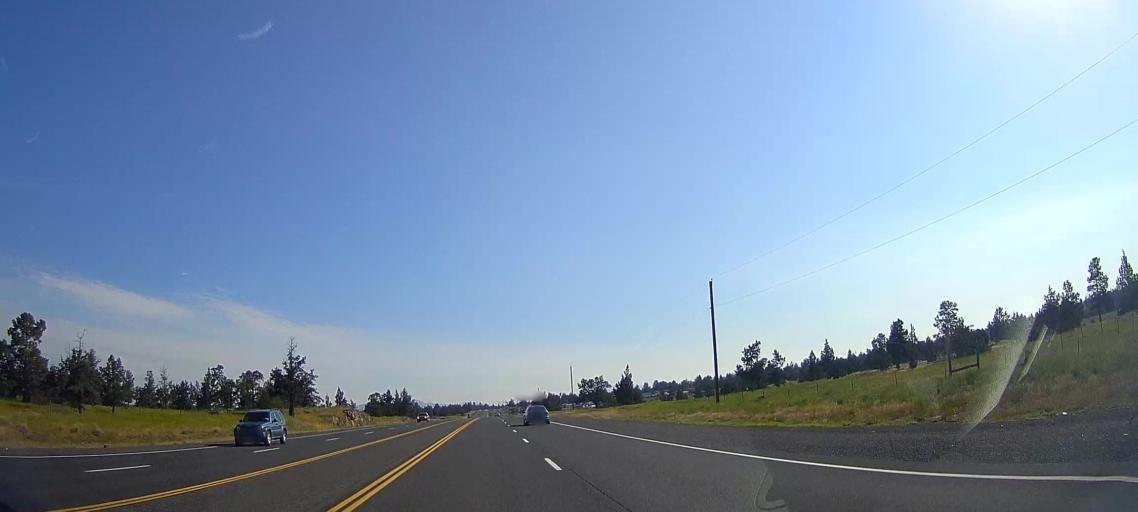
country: US
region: Oregon
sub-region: Deschutes County
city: Redmond
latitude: 44.2165
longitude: -121.2161
